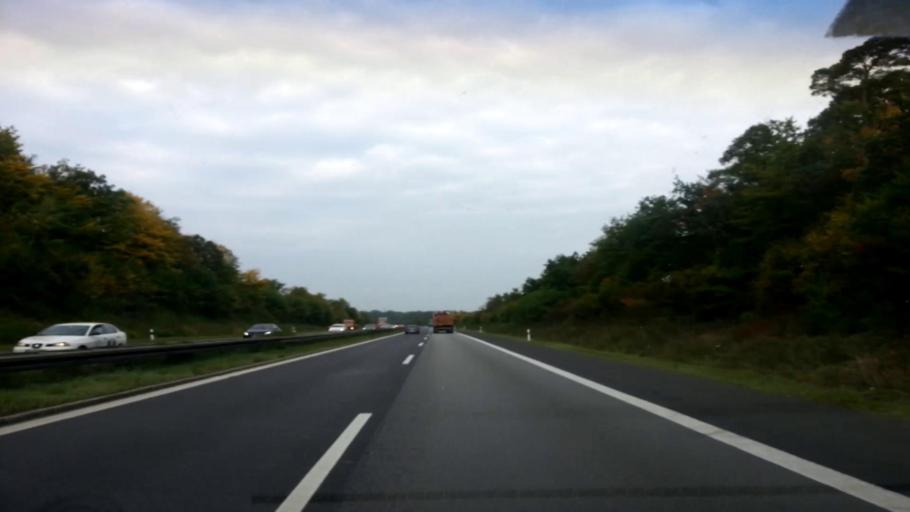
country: DE
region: Bavaria
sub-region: Regierungsbezirk Unterfranken
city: Knetzgau
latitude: 49.9953
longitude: 10.5209
